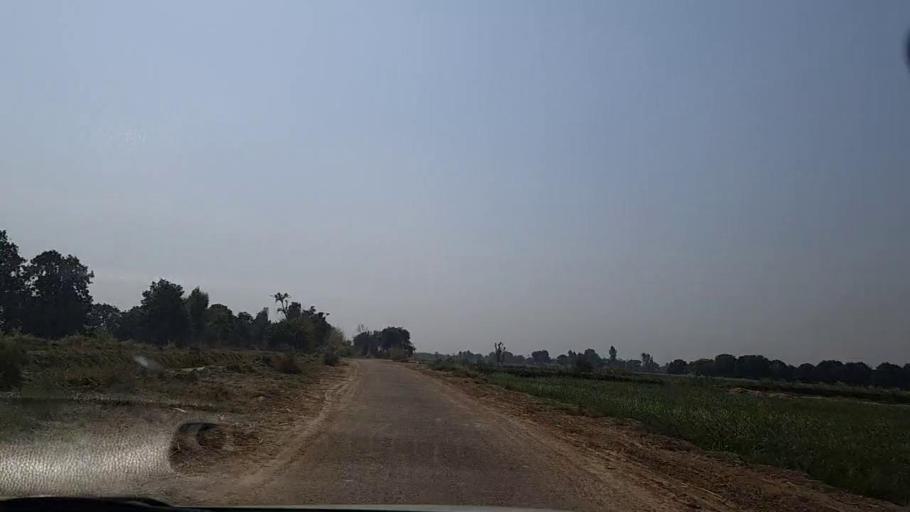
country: PK
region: Sindh
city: Mirpur Khas
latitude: 25.4899
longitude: 69.1964
